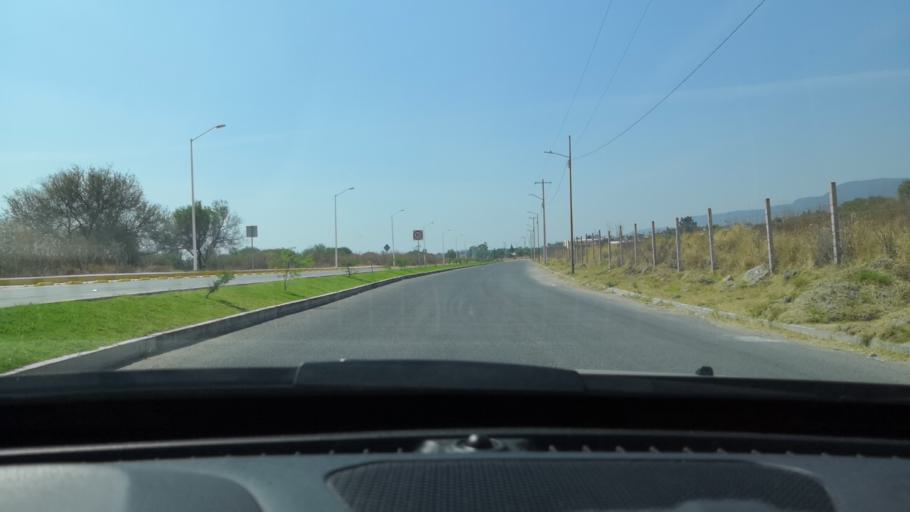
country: MX
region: Guanajuato
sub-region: Purisima del Rincon
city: Potrerillos (Guanajal)
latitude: 21.0545
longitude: -101.8681
